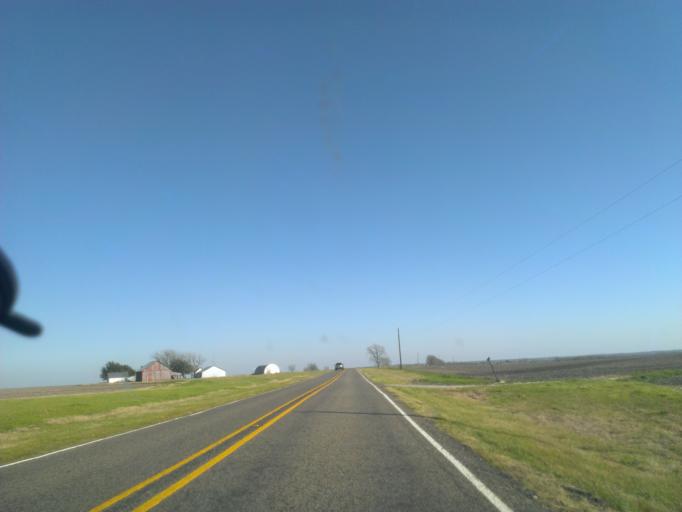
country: US
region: Texas
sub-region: Milam County
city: Thorndale
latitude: 30.5521
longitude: -97.2897
